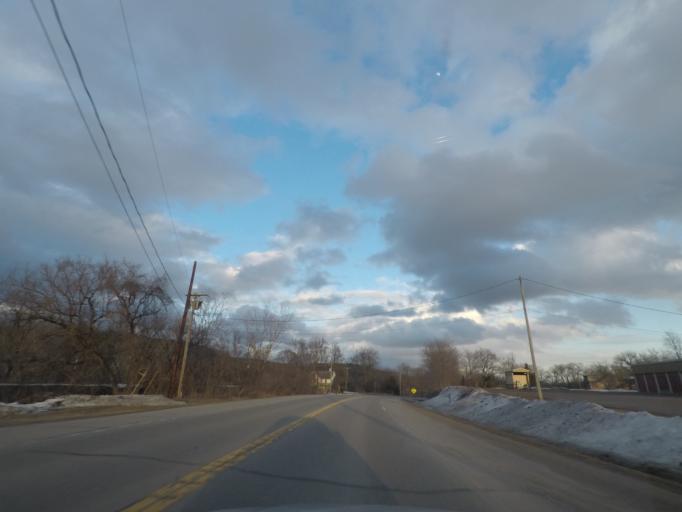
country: US
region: New York
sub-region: Montgomery County
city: Saint Johnsville
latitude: 43.0032
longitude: -74.7070
